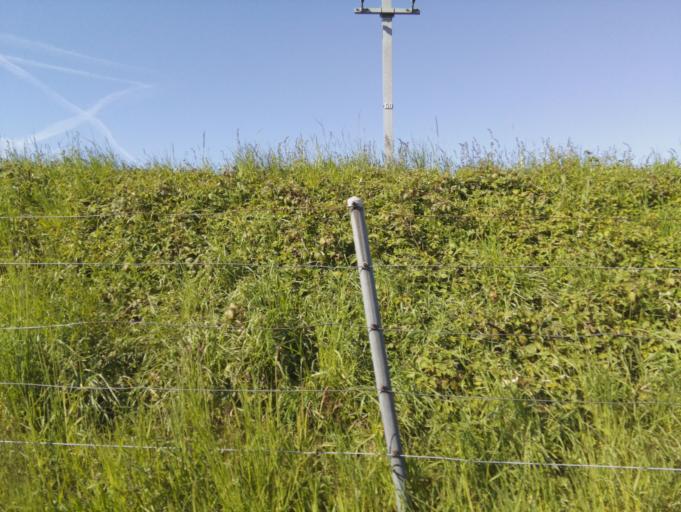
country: CH
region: Saint Gallen
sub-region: Wahlkreis See-Gaster
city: Jona
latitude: 47.2221
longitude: 8.8613
